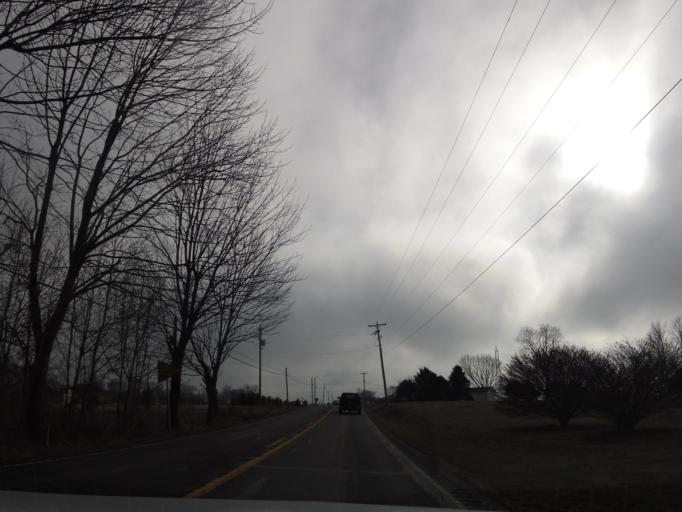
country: US
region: Indiana
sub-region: Jefferson County
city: North Madison
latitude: 38.7871
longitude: -85.4307
